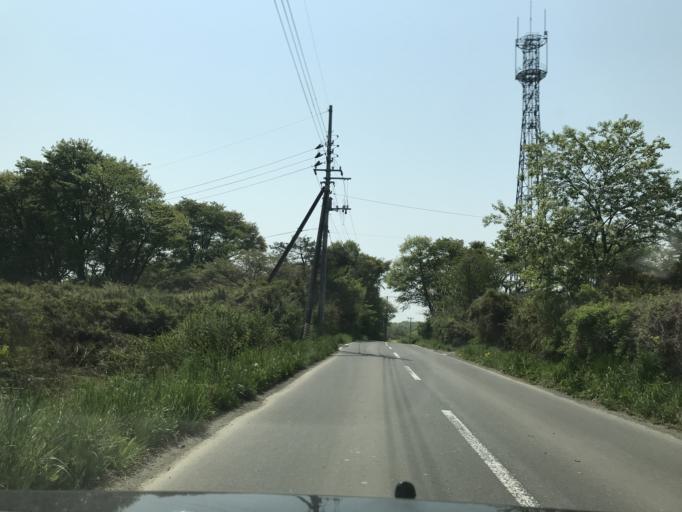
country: JP
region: Iwate
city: Ichinoseki
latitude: 38.8526
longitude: 141.0552
